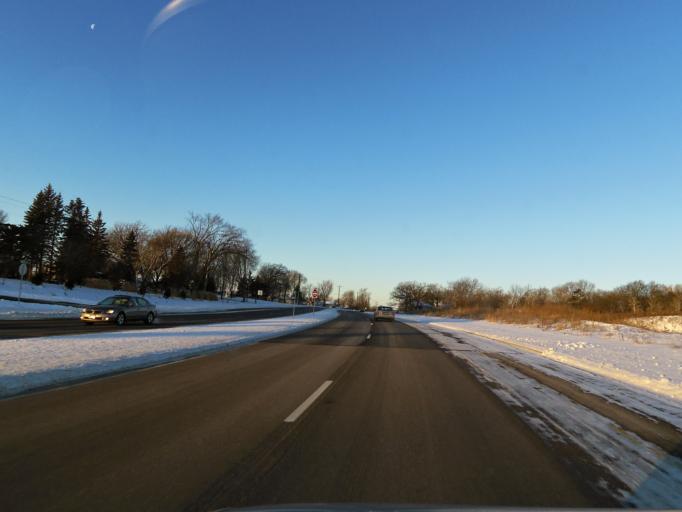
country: US
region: Minnesota
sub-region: Scott County
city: Prior Lake
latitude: 44.7176
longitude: -93.3934
